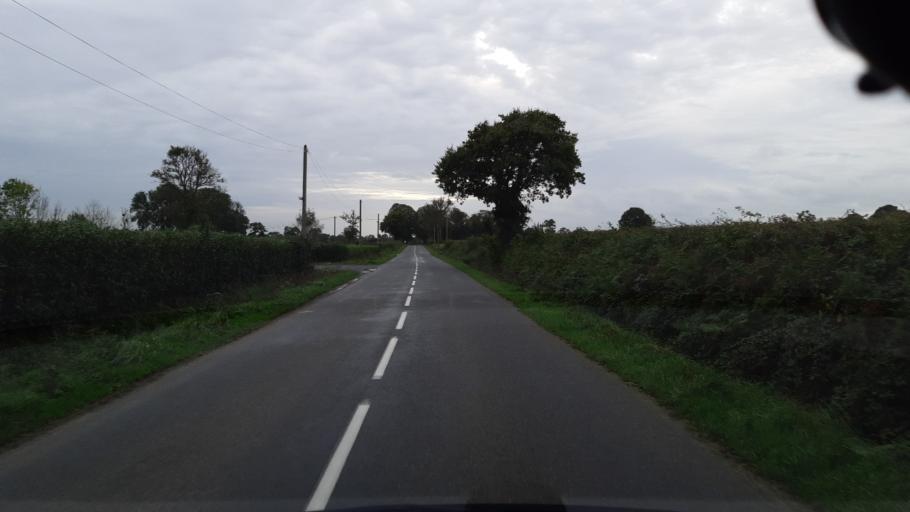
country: FR
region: Lower Normandy
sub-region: Departement de la Manche
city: Hambye
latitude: 48.9736
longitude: -1.2480
